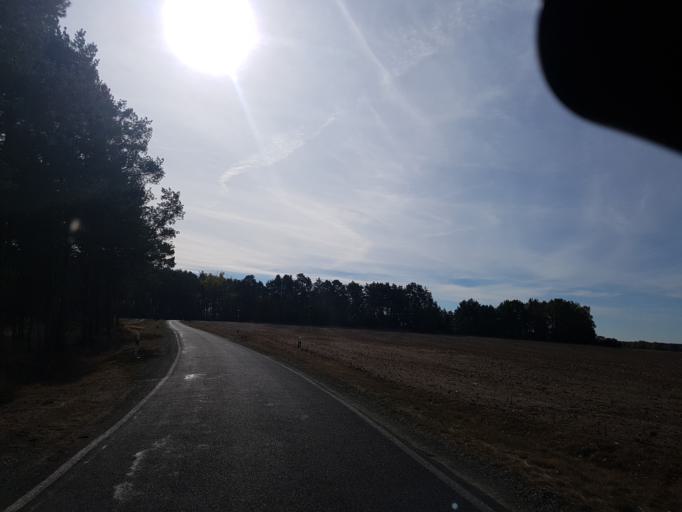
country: DE
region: Brandenburg
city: Schlieben
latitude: 51.7871
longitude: 13.3206
